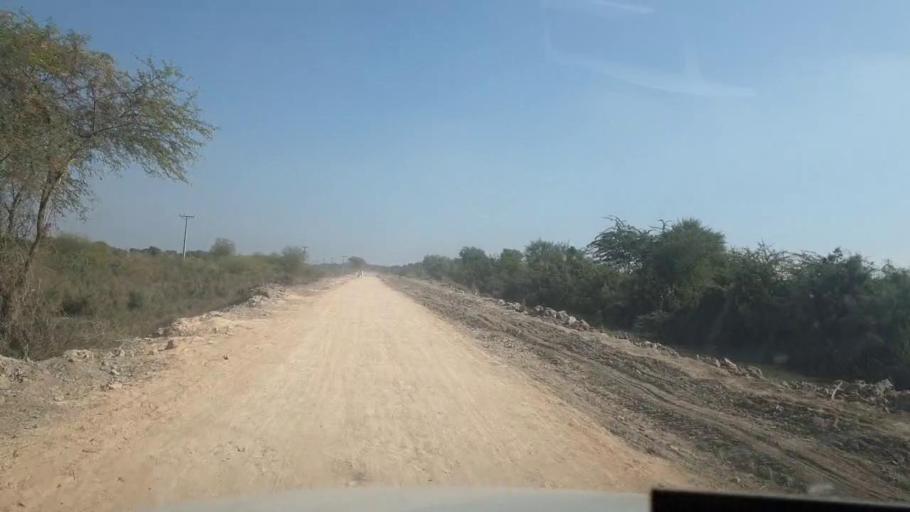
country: PK
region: Sindh
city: Kotri
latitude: 25.1623
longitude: 68.3005
